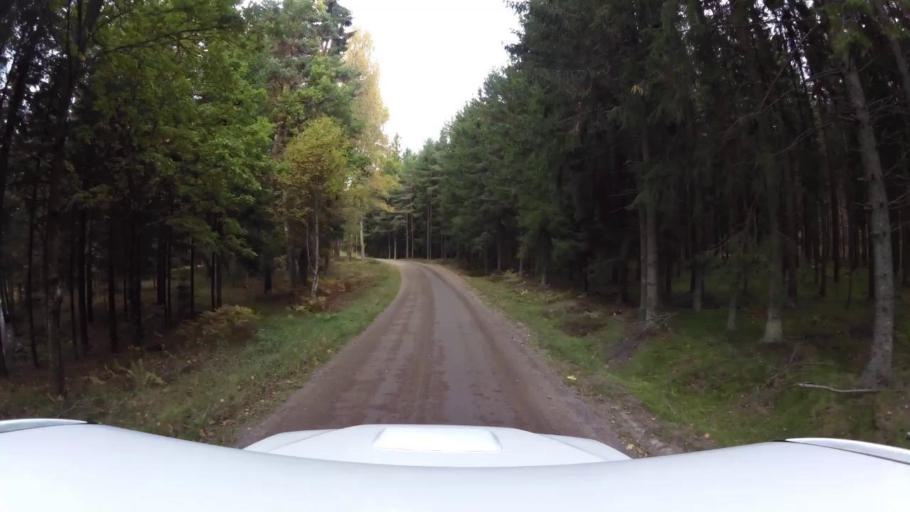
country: SE
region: OEstergoetland
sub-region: Linkopings Kommun
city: Ekangen
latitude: 58.5498
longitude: 15.6742
